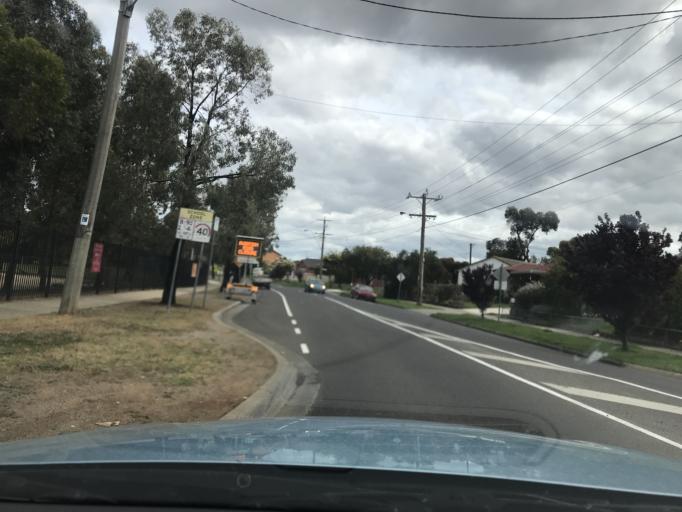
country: AU
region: Victoria
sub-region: Hobsons Bay
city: Laverton
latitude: -37.8563
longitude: 144.7720
